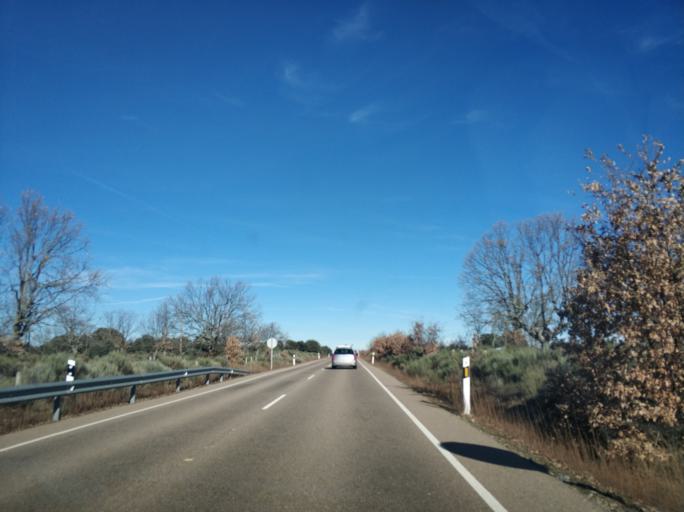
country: ES
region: Castille and Leon
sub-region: Provincia de Salamanca
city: Herguijuela del Campo
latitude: 40.6305
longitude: -5.9054
